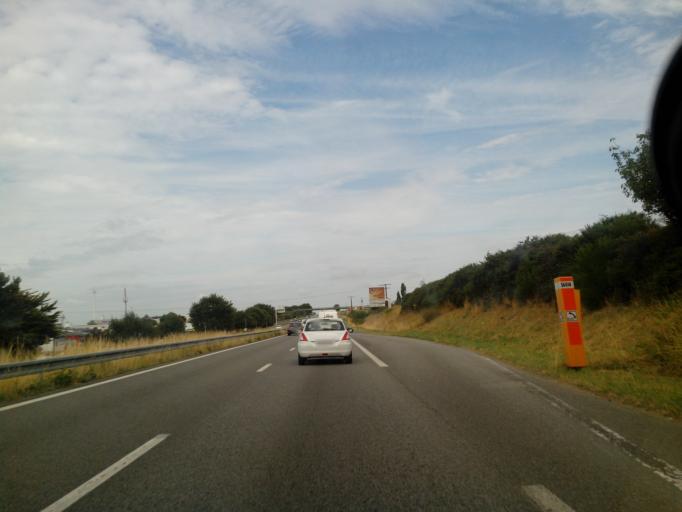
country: FR
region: Brittany
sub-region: Departement du Morbihan
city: Theix
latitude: 47.6342
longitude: -2.6598
